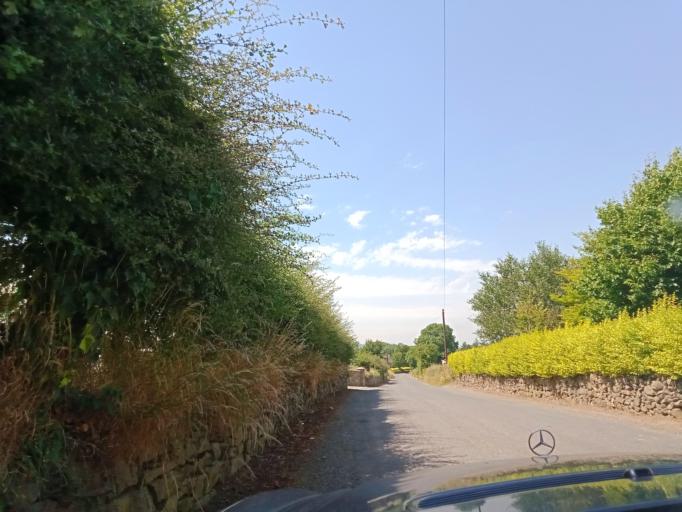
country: IE
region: Leinster
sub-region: Kilkenny
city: Mooncoin
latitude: 52.2743
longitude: -7.2336
